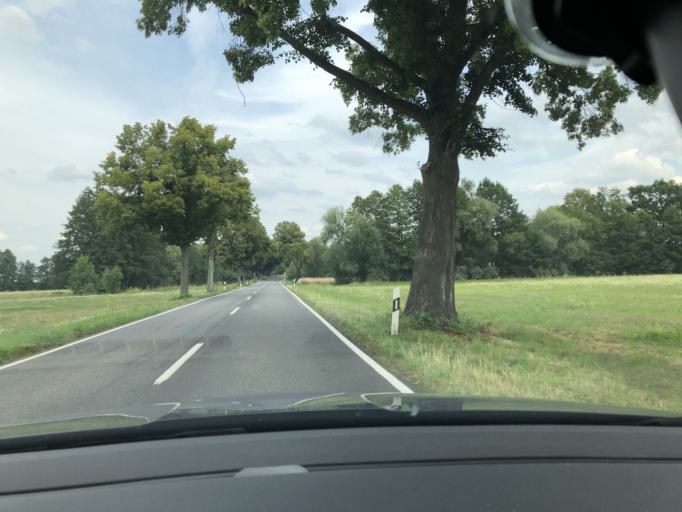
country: DE
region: Brandenburg
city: Kasel-Golzig
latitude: 51.9665
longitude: 13.7507
